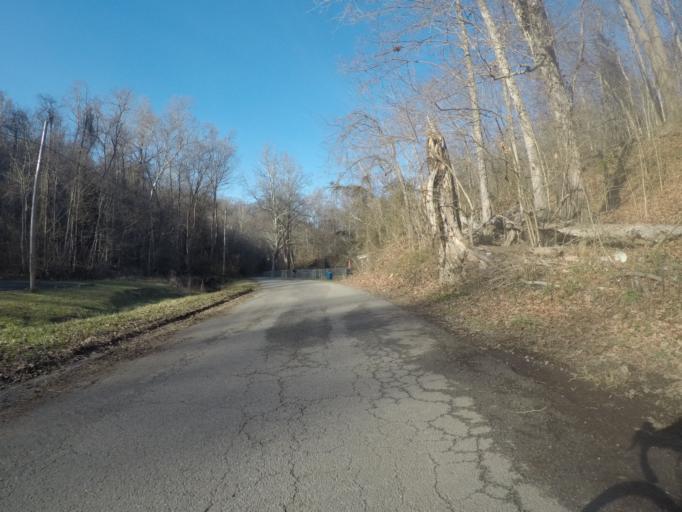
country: US
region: West Virginia
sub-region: Cabell County
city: Huntington
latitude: 38.3934
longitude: -82.4859
